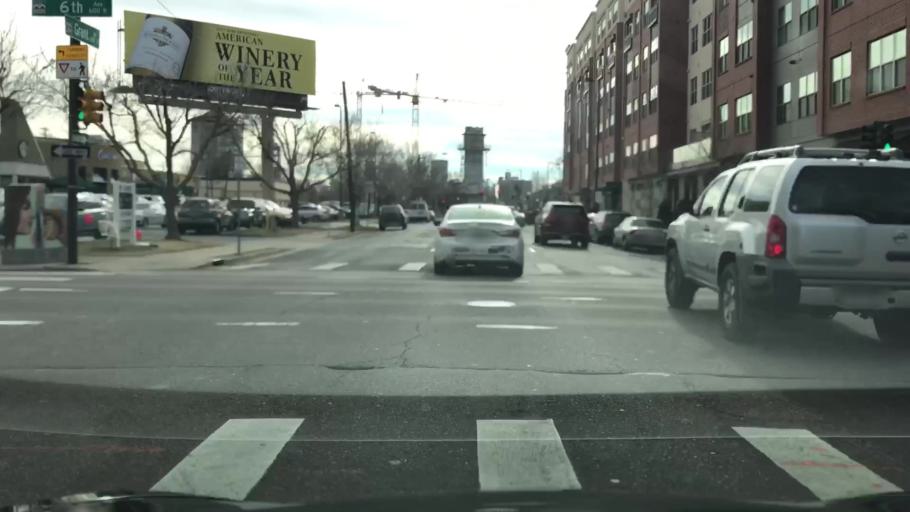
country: US
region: Colorado
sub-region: Denver County
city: Denver
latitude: 39.7257
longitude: -104.9837
